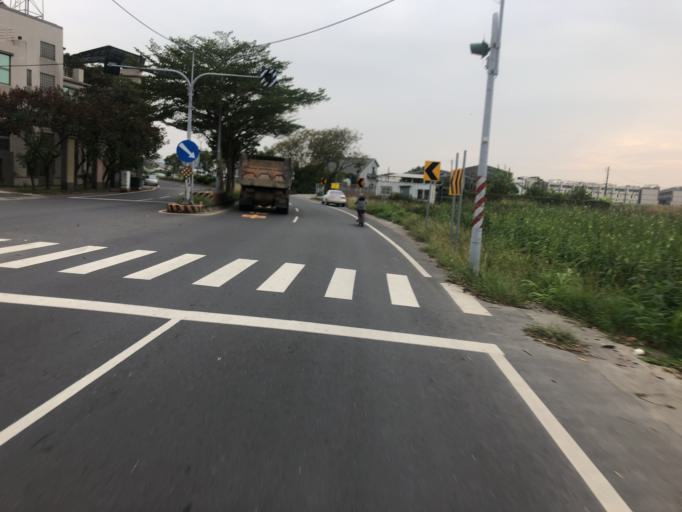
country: TW
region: Taiwan
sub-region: Tainan
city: Tainan
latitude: 23.1373
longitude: 120.2868
